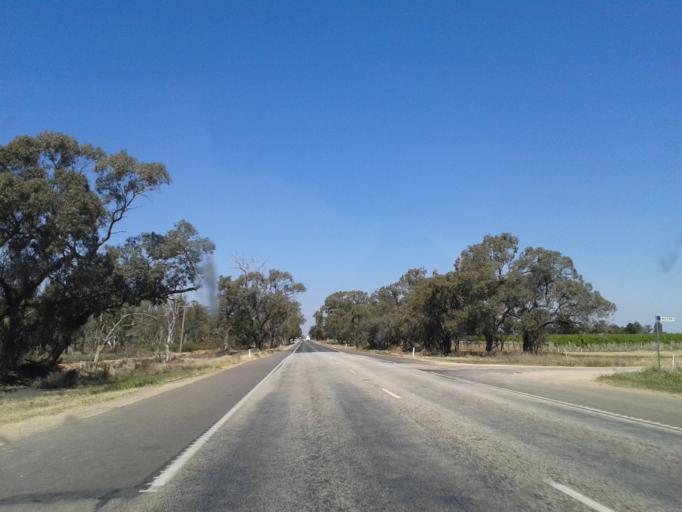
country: AU
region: Victoria
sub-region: Swan Hill
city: Swan Hill
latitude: -35.2019
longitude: 143.3936
